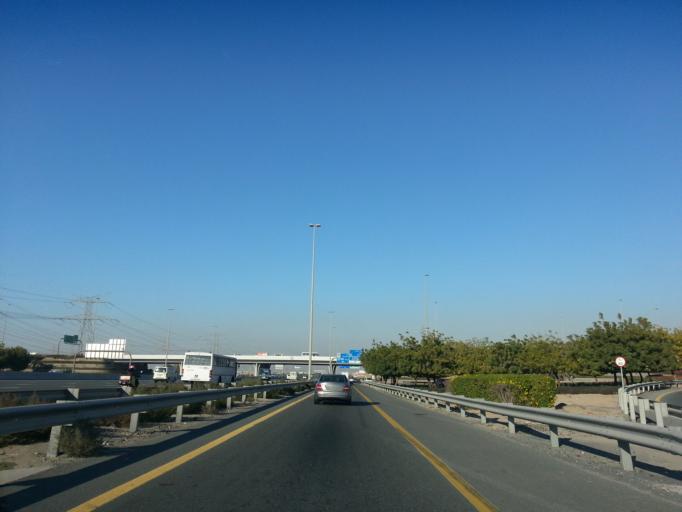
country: AE
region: Dubai
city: Dubai
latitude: 25.0749
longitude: 55.2093
